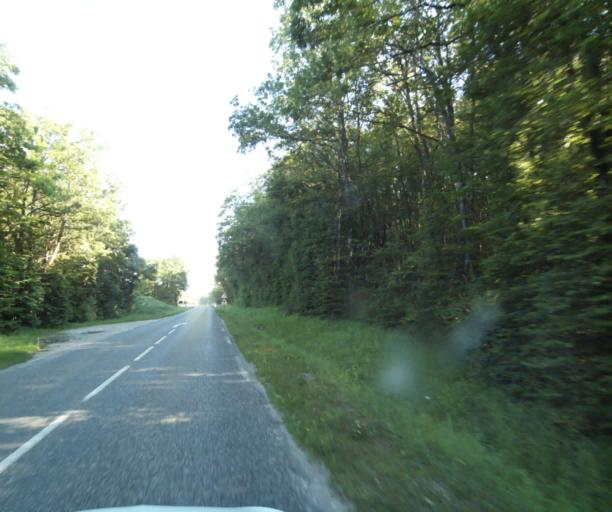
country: FR
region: Rhone-Alpes
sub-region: Departement de la Haute-Savoie
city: Messery
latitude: 46.3275
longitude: 6.2923
